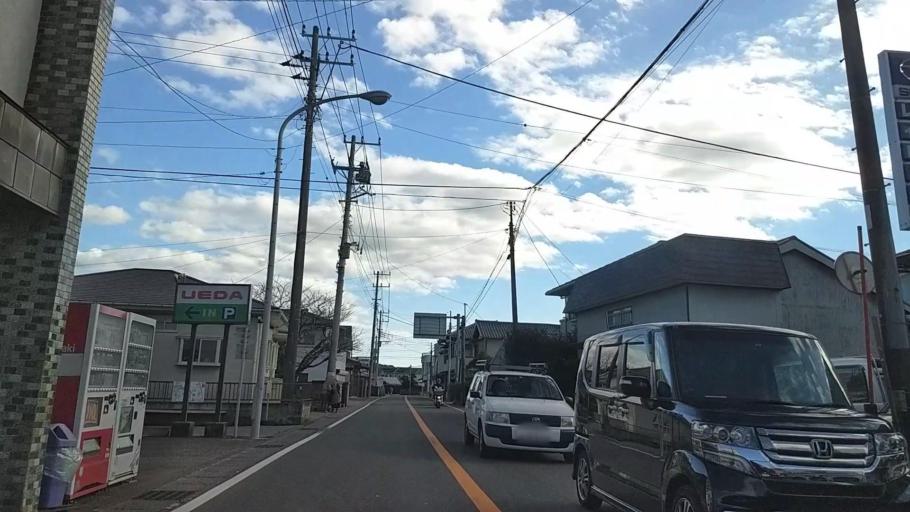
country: JP
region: Chiba
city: Tateyama
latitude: 35.0240
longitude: 139.8598
